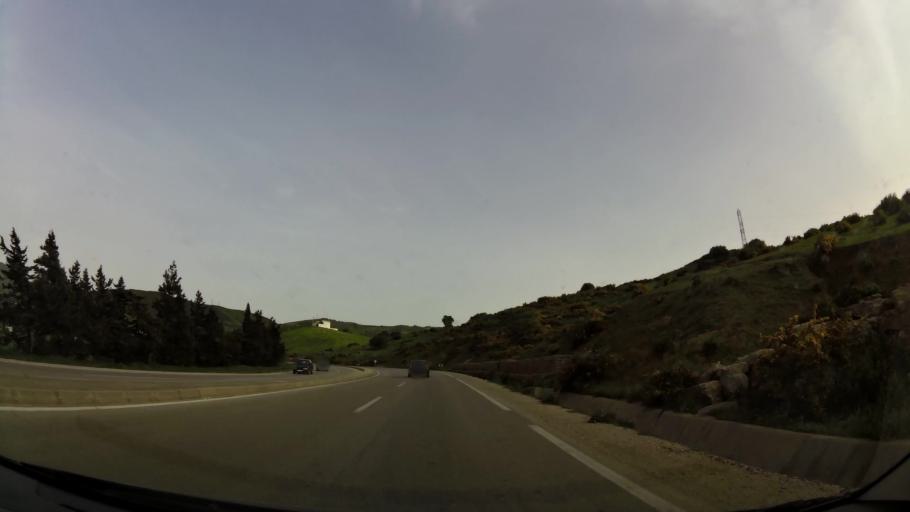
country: MA
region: Tanger-Tetouan
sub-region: Tanger-Assilah
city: Dar Chaoui
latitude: 35.5643
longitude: -5.6055
